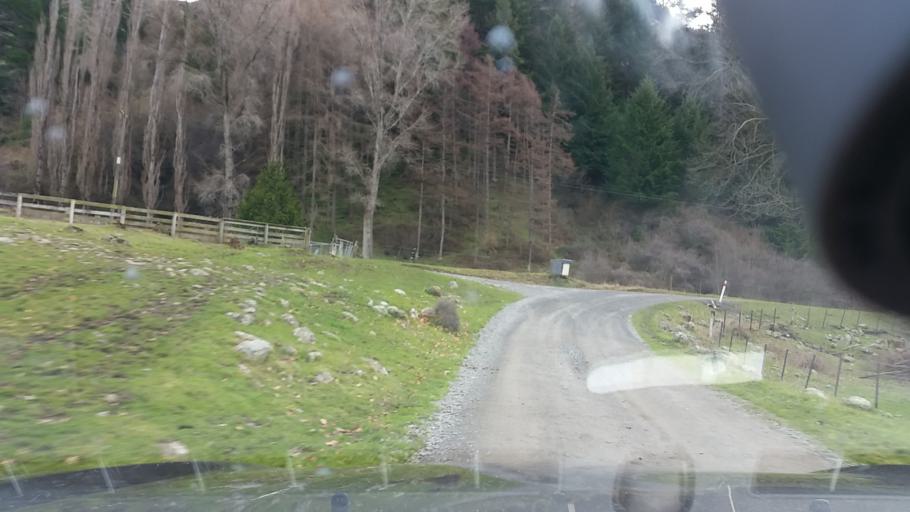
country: NZ
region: Tasman
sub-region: Tasman District
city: Richmond
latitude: -41.7269
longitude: 173.4700
